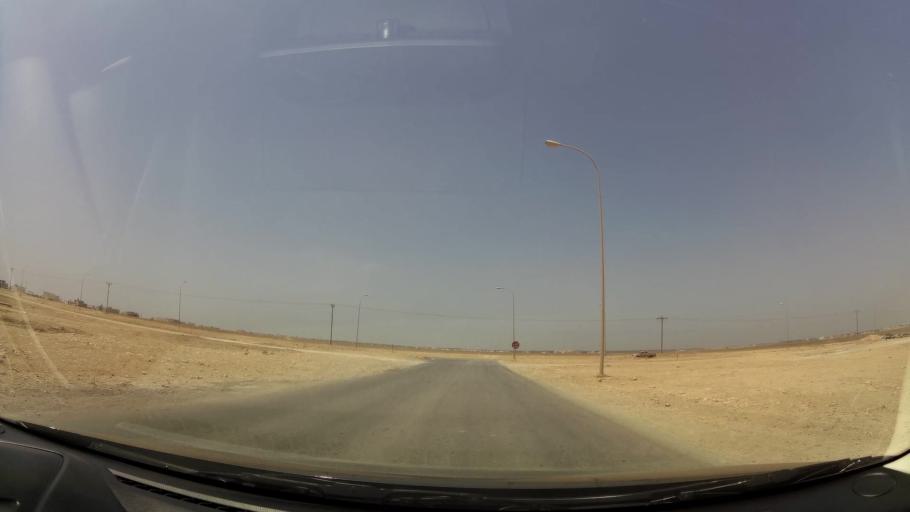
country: OM
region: Zufar
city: Salalah
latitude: 17.0692
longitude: 54.2055
